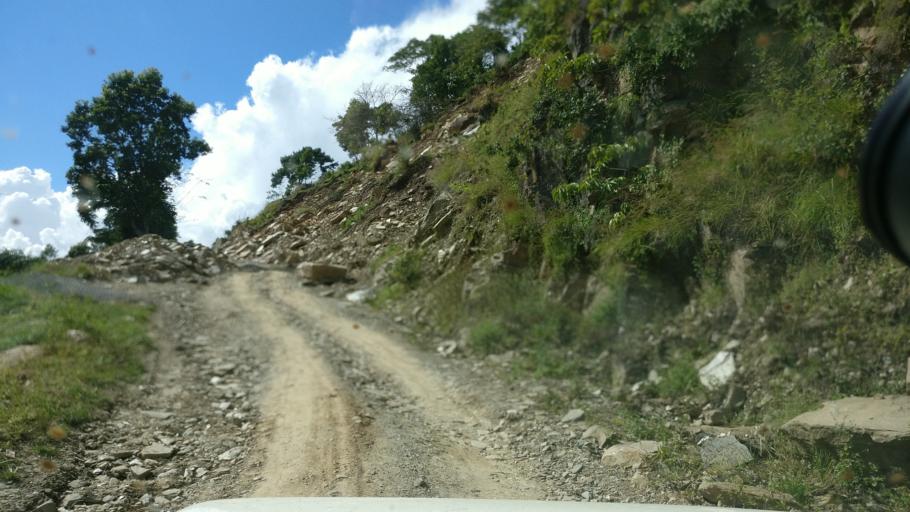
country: NP
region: Western Region
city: Baglung
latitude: 28.2634
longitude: 83.6422
